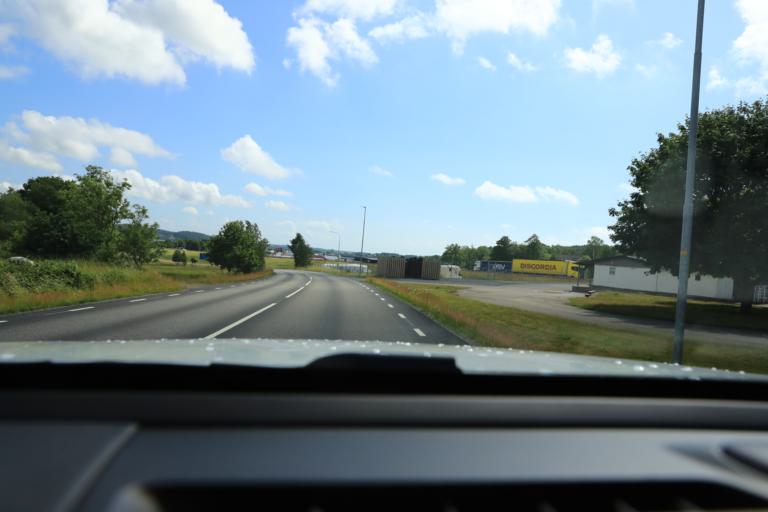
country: SE
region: Halland
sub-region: Varbergs Kommun
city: Varberg
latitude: 57.1743
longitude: 12.2779
